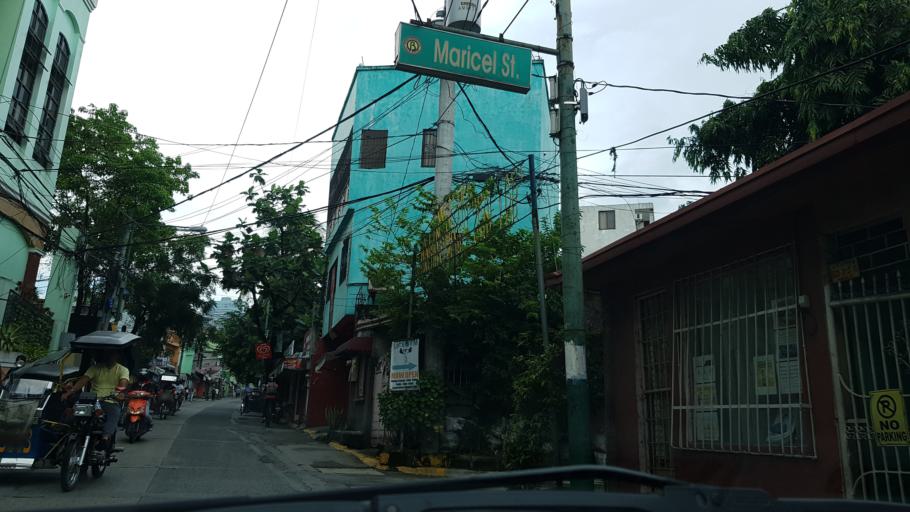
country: PH
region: Calabarzon
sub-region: Province of Rizal
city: Pateros
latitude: 14.5435
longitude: 121.0582
